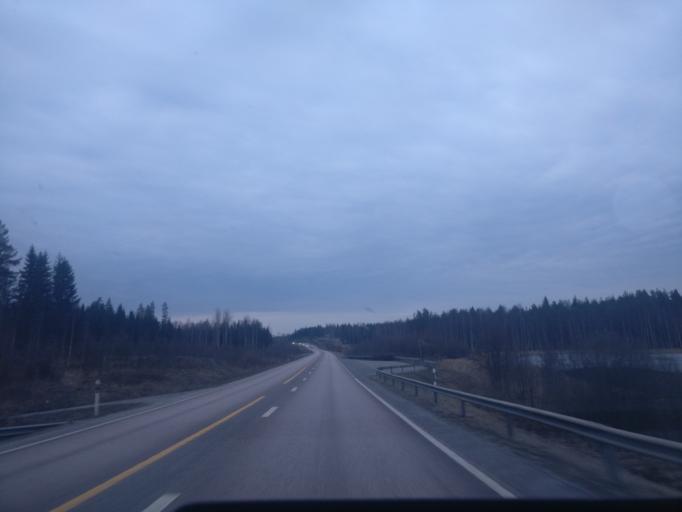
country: FI
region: Paijanne Tavastia
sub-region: Lahti
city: Heinola
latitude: 61.3395
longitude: 26.0423
